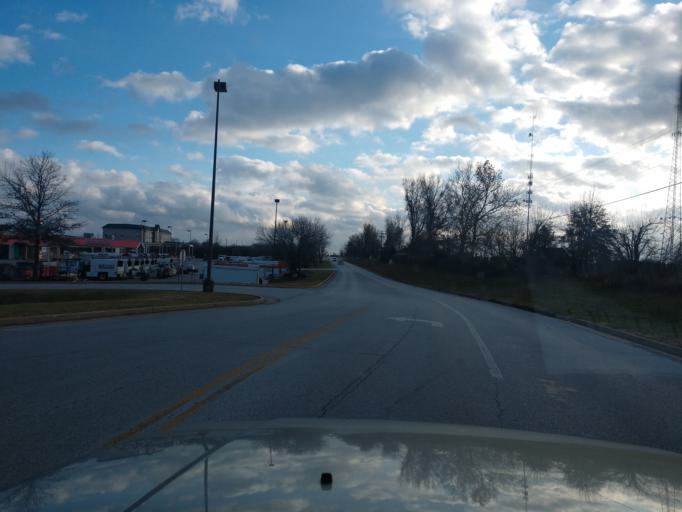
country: US
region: Illinois
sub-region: Adams County
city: Quincy
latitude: 39.9345
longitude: -91.3300
